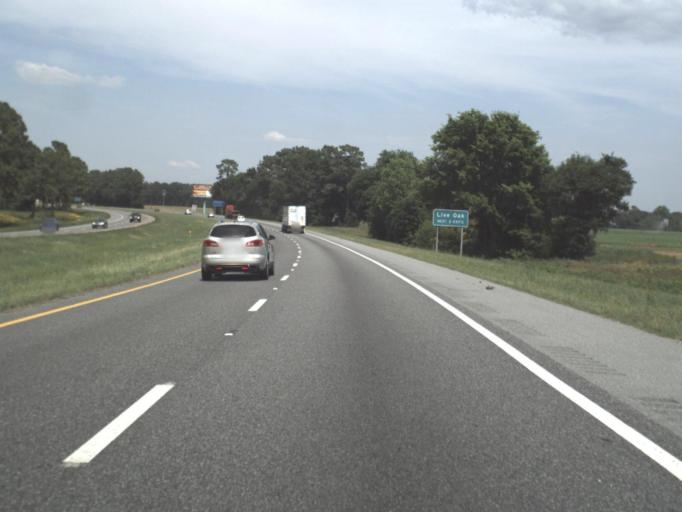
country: US
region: Florida
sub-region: Suwannee County
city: Live Oak
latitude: 30.3370
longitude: -83.1040
